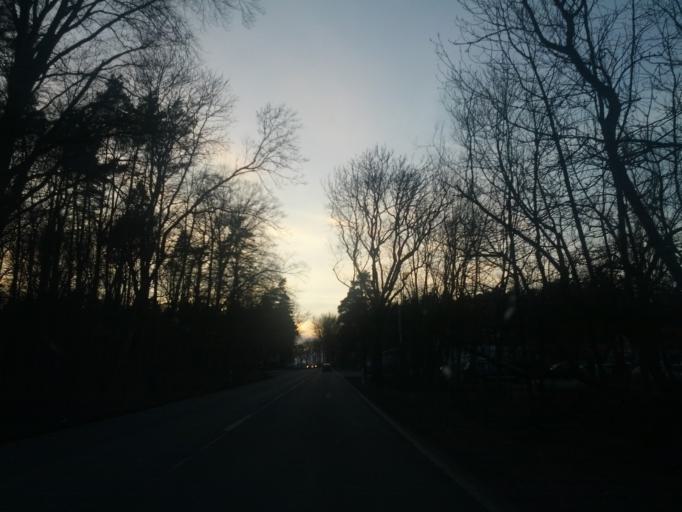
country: DE
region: Thuringia
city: Oberdorla
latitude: 51.2084
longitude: 10.3745
